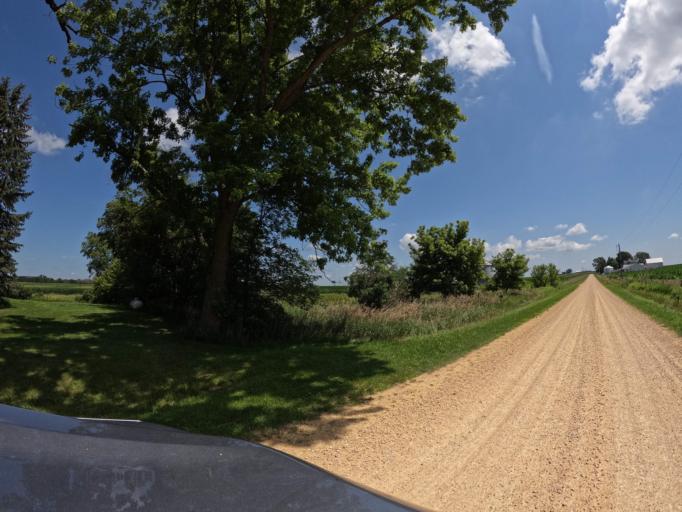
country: US
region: Iowa
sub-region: Clinton County
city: De Witt
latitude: 41.7783
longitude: -90.4217
